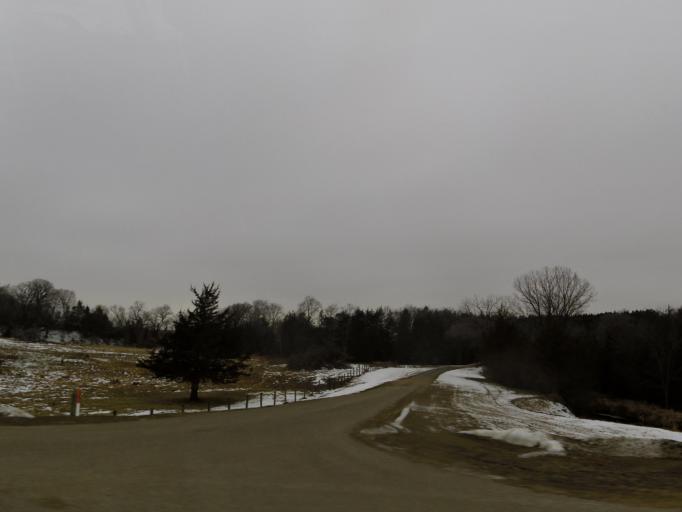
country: US
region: Minnesota
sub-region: Carver County
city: Carver
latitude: 44.7404
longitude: -93.6842
